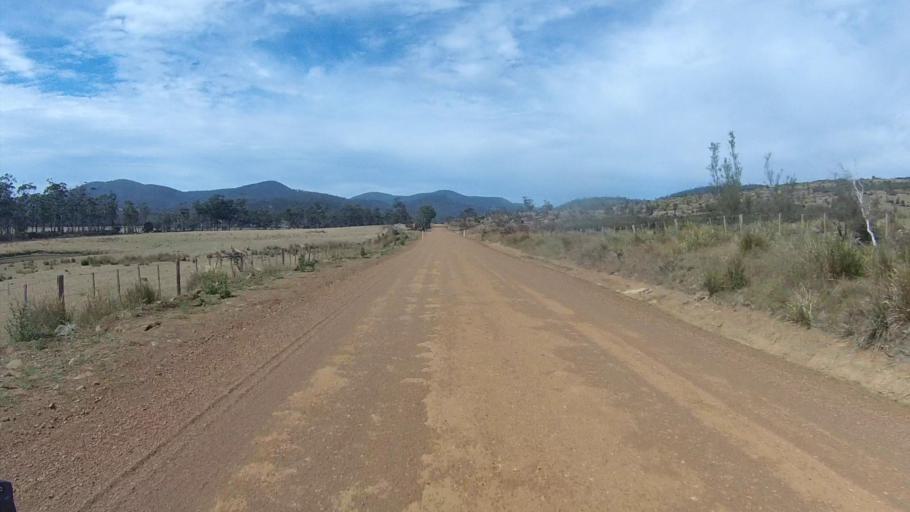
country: AU
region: Tasmania
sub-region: Sorell
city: Sorell
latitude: -42.6292
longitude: 147.9020
